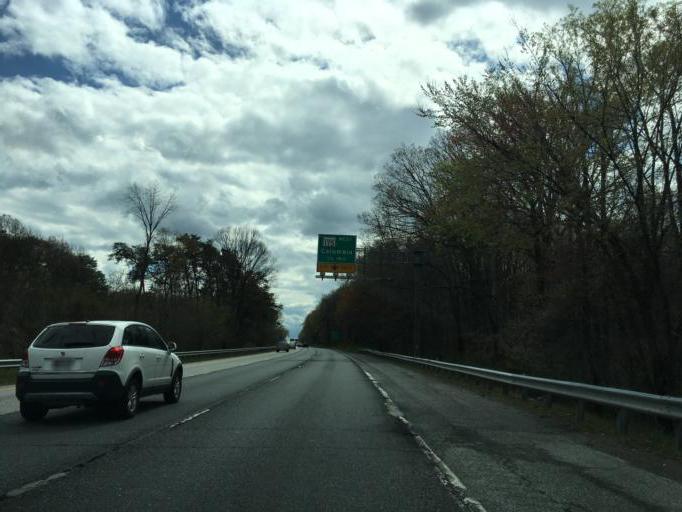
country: US
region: Maryland
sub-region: Anne Arundel County
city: Jessup
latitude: 39.1506
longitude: -76.7511
